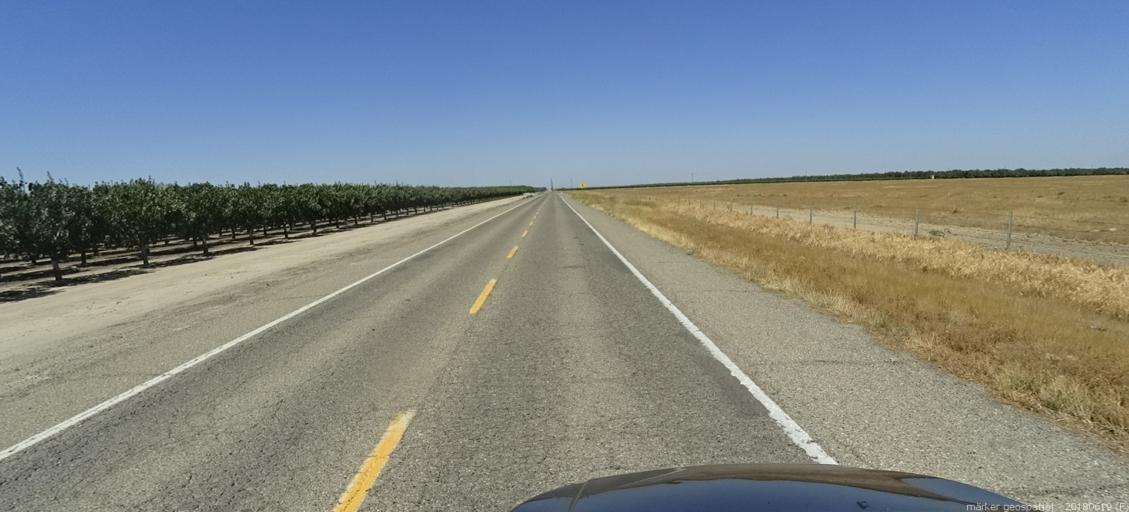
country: US
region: California
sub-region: Fresno County
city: Mendota
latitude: 36.8510
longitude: -120.2493
